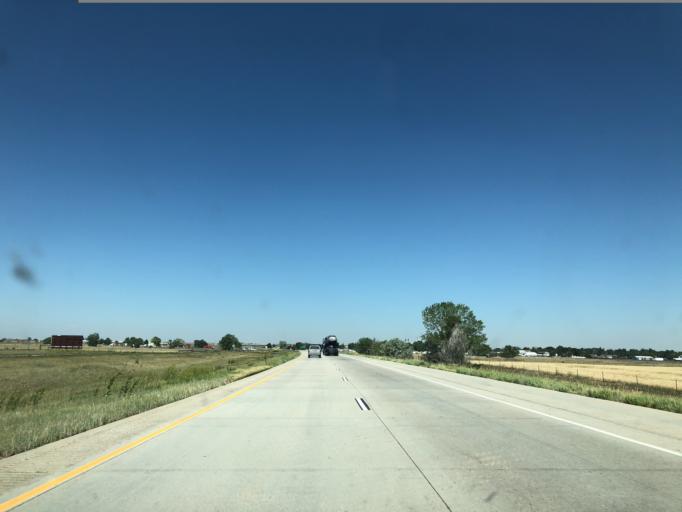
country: US
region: Colorado
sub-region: Adams County
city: Strasburg
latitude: 39.7332
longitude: -104.3113
